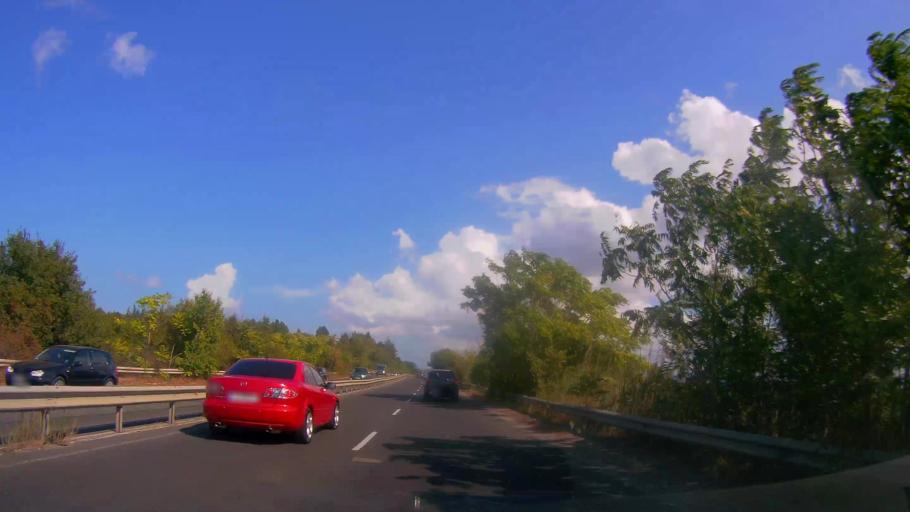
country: BG
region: Burgas
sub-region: Obshtina Burgas
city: Burgas
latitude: 42.4431
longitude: 27.4665
